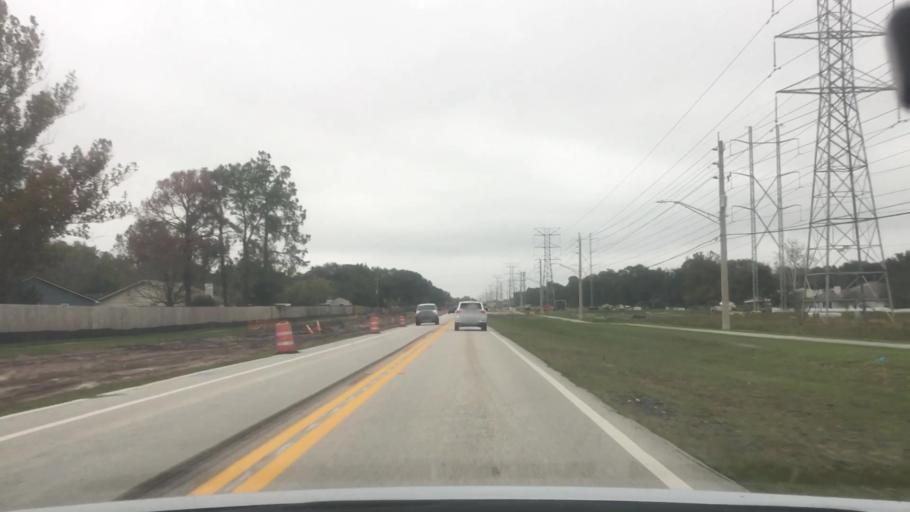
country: US
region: Florida
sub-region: Duval County
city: Atlantic Beach
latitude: 30.3484
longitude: -81.4899
